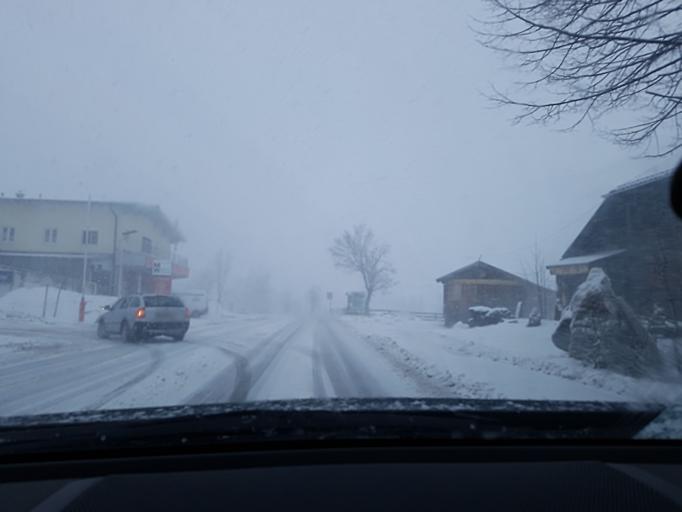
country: AT
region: Salzburg
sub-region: Politischer Bezirk Hallein
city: Abtenau
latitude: 47.5665
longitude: 13.3405
